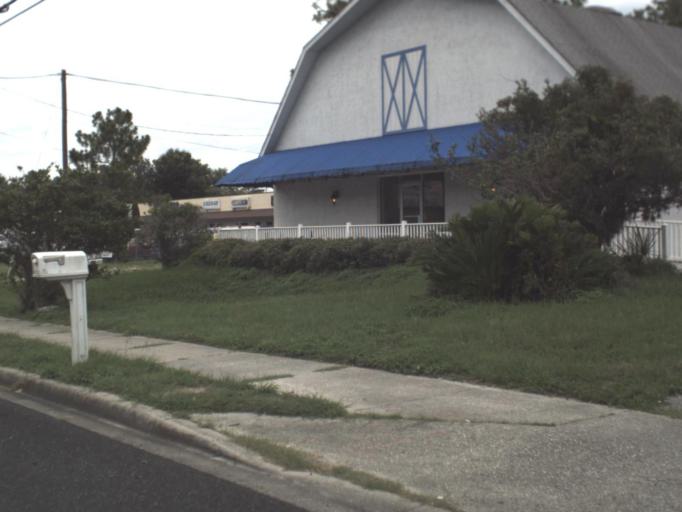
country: US
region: Florida
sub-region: Citrus County
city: Inverness Highlands North
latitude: 28.8526
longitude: -82.3841
